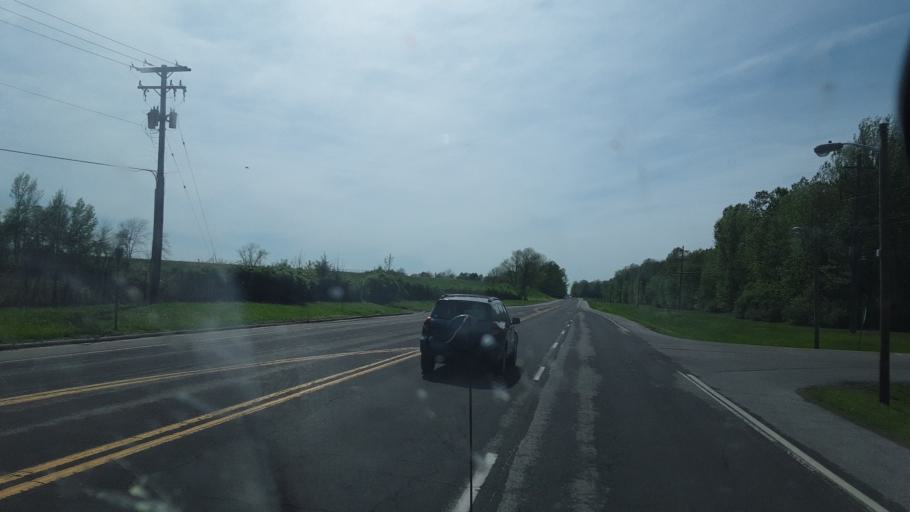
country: US
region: Illinois
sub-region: Jackson County
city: Carbondale
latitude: 37.7005
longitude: -89.2213
